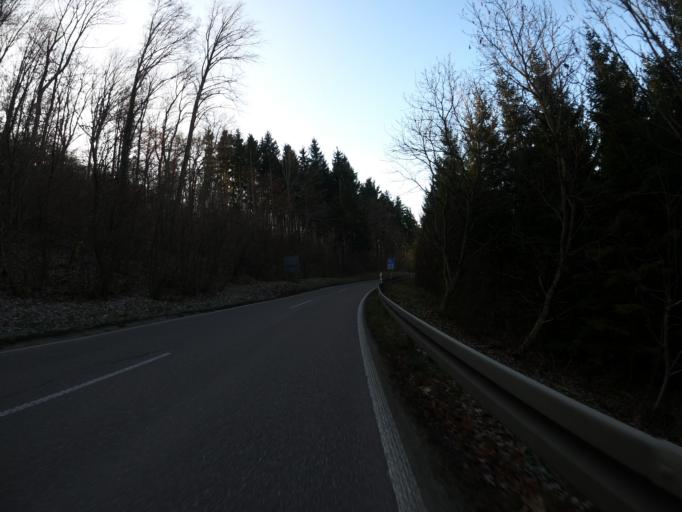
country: DE
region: Baden-Wuerttemberg
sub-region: Regierungsbezirk Stuttgart
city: Gammelshausen
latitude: 48.6329
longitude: 9.6566
